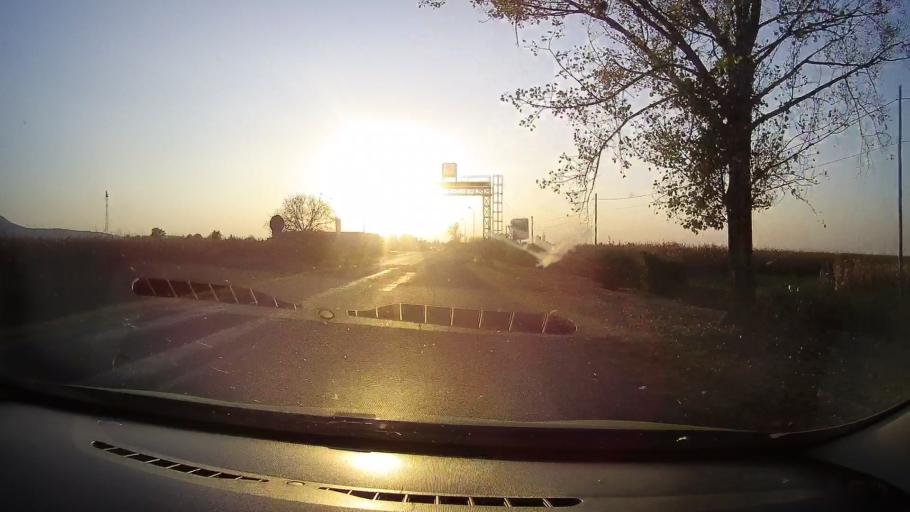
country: RO
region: Arad
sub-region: Comuna Ineu
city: Ineu
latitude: 46.4283
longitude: 21.8670
